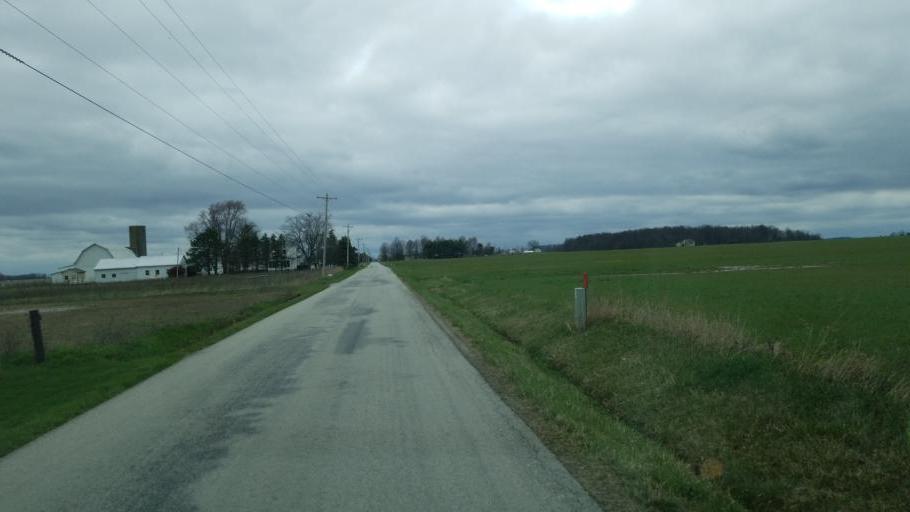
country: US
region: Ohio
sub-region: Delaware County
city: Delaware
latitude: 40.3735
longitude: -83.1198
